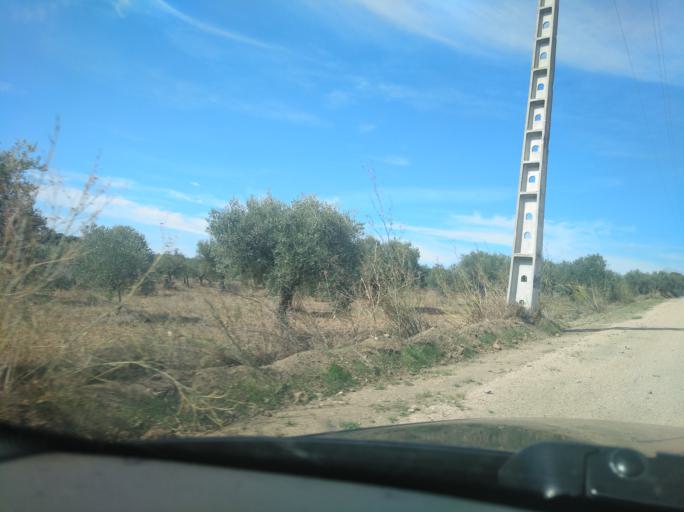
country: PT
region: Portalegre
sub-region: Campo Maior
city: Campo Maior
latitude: 39.0486
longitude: -7.0511
